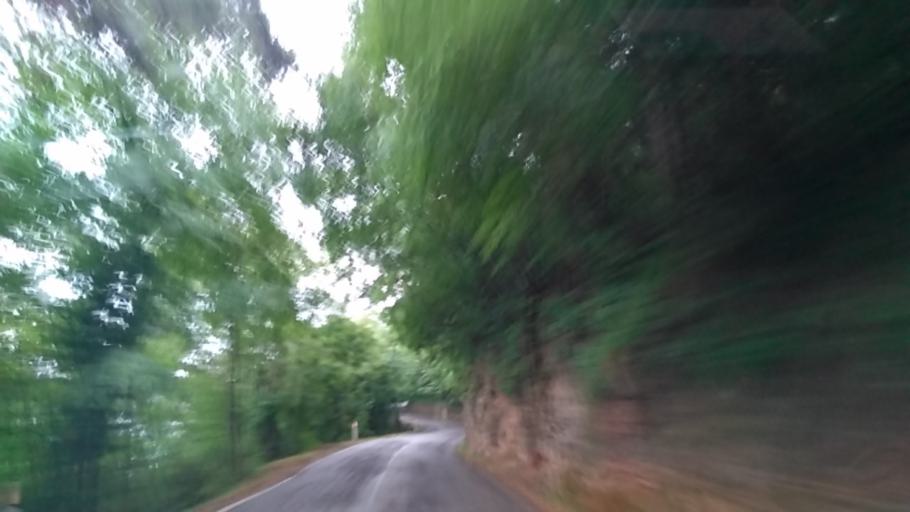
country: IT
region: Lombardy
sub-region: Provincia di Brescia
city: Gardola
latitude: 45.7642
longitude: 10.7183
